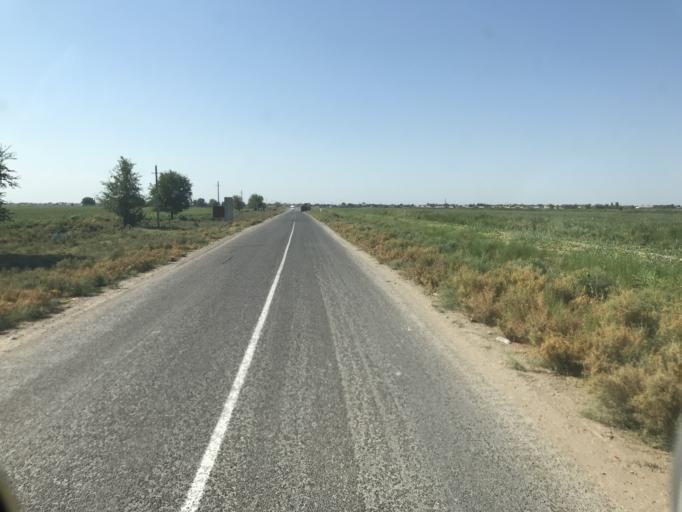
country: KZ
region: Ongtustik Qazaqstan
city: Myrzakent
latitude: 40.6824
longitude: 68.5567
